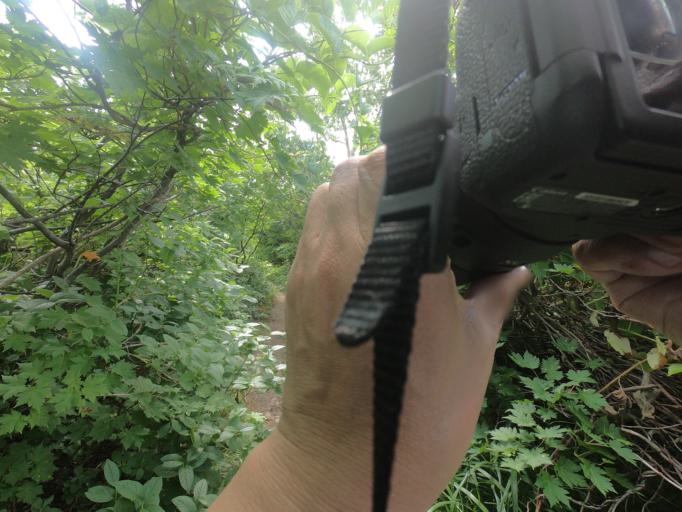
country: JP
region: Akita
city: Yuzawa
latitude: 38.9740
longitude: 140.7764
